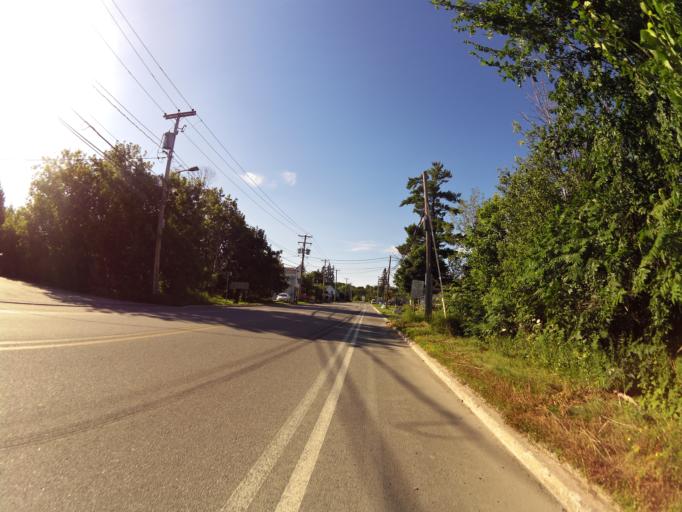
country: CA
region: Quebec
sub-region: Outaouais
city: Gatineau
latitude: 45.5050
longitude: -75.7837
